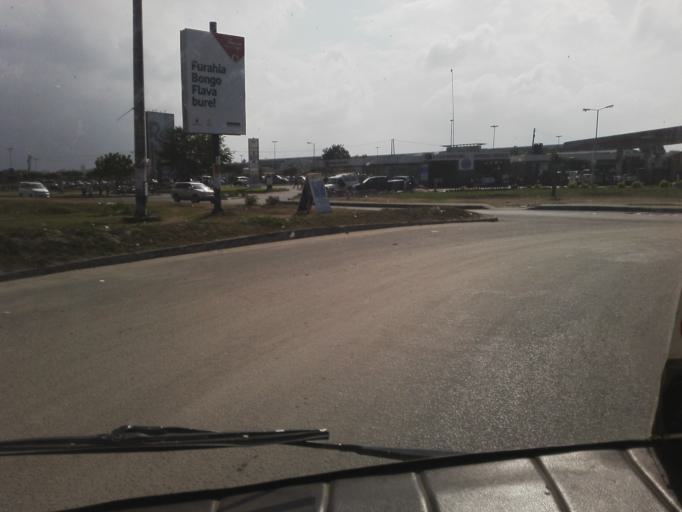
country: TZ
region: Dar es Salaam
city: Magomeni
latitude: -6.7727
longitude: 39.2222
